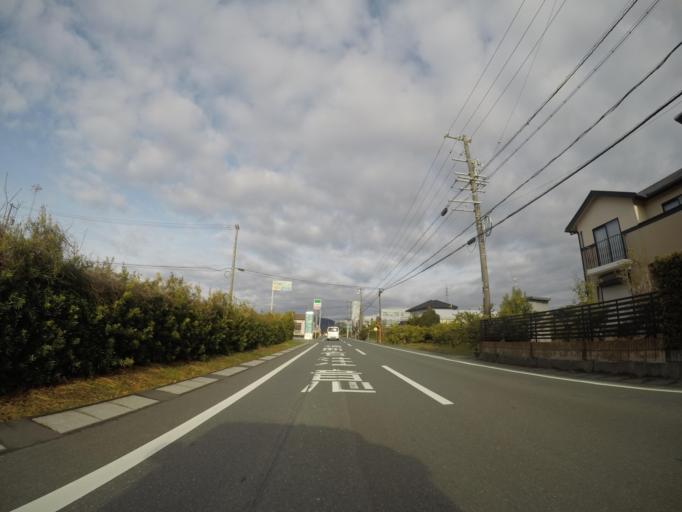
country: JP
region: Shizuoka
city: Hamakita
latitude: 34.8230
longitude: 137.7462
